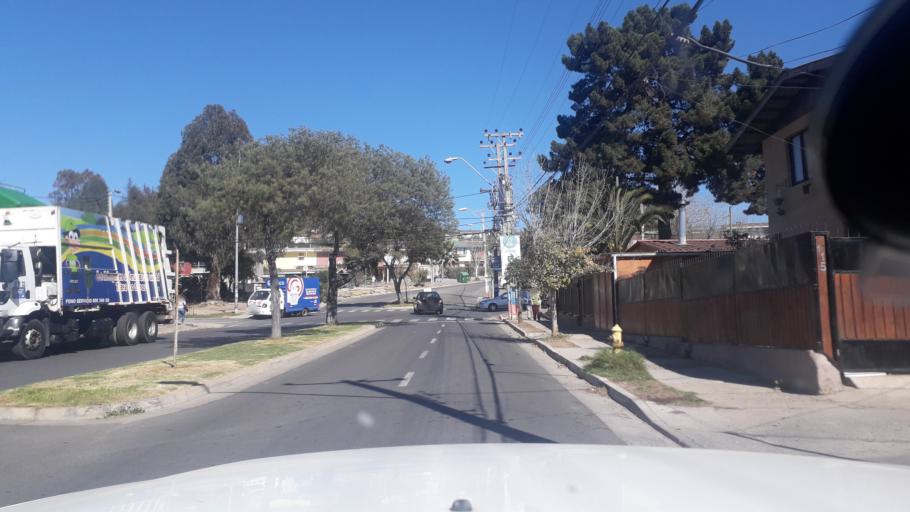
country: CL
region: Valparaiso
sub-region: Provincia de Valparaiso
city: Vina del Mar
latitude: -33.0385
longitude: -71.5079
